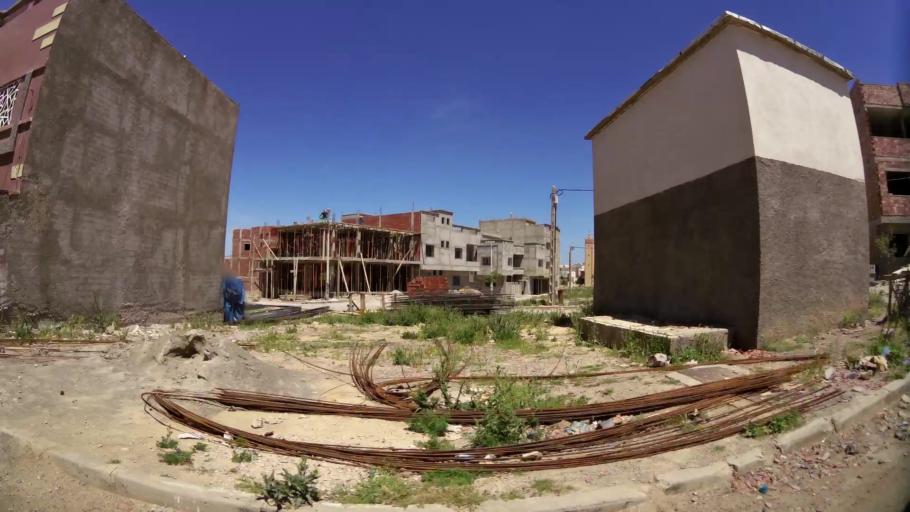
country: MA
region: Oriental
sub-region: Oujda-Angad
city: Oujda
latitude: 34.6528
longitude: -1.9215
